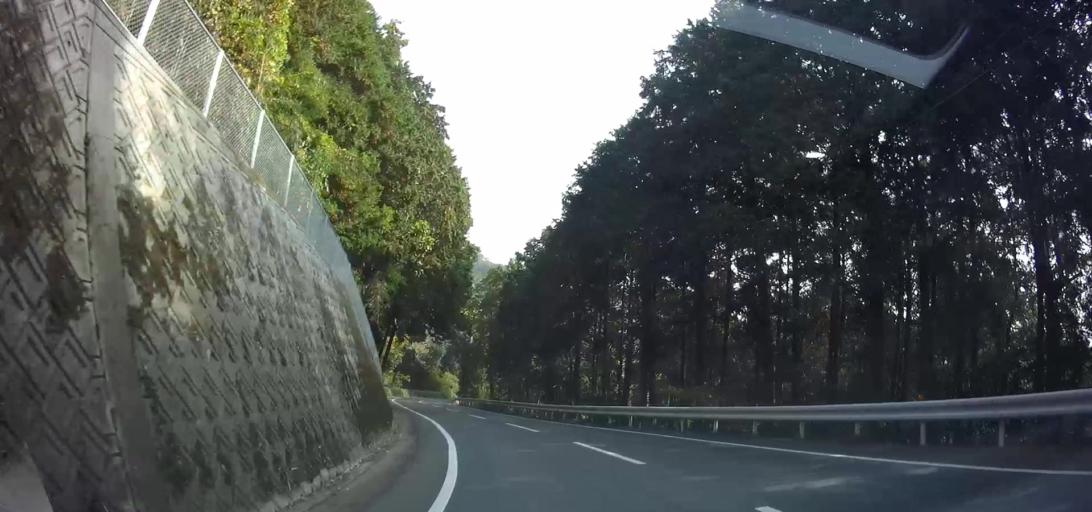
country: JP
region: Nagasaki
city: Shimabara
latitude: 32.6754
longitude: 130.2096
